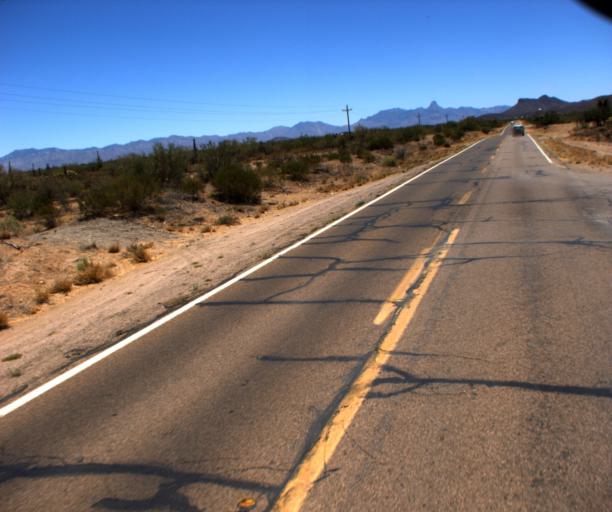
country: US
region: Arizona
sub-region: Pima County
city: Sells
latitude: 31.9341
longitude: -111.9124
